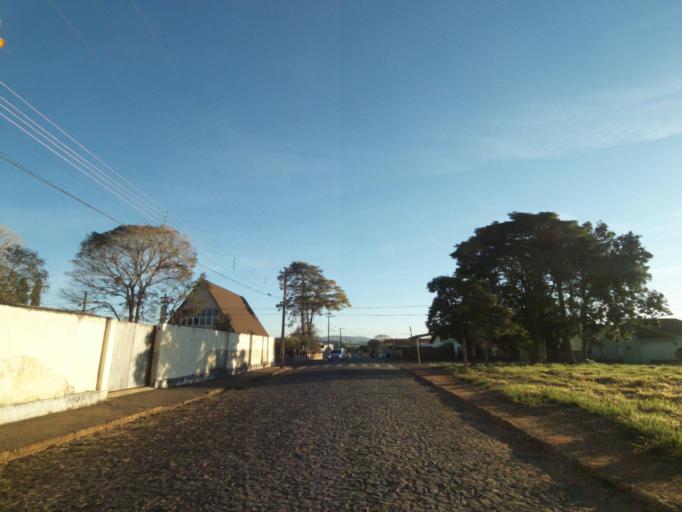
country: BR
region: Parana
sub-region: Tibagi
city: Tibagi
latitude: -24.5102
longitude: -50.4128
